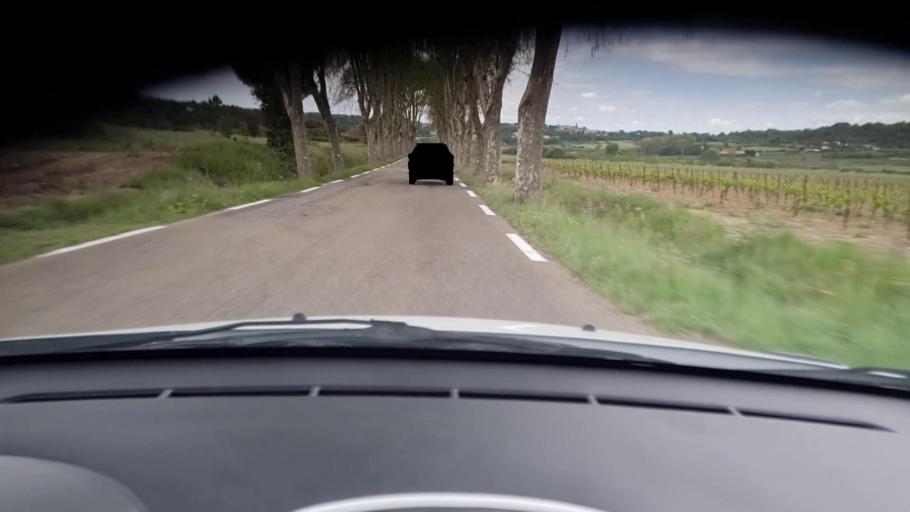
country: FR
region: Languedoc-Roussillon
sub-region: Departement du Gard
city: Blauzac
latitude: 43.9713
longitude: 4.3939
